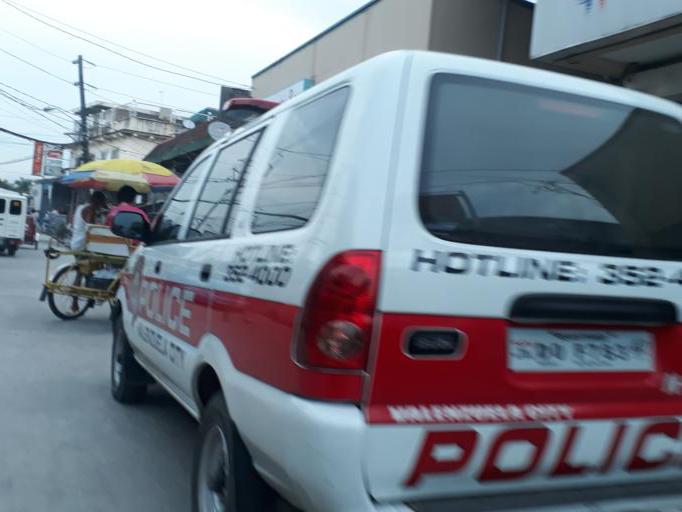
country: PH
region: Central Luzon
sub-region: Province of Bulacan
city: Obando
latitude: 14.7087
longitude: 120.9469
